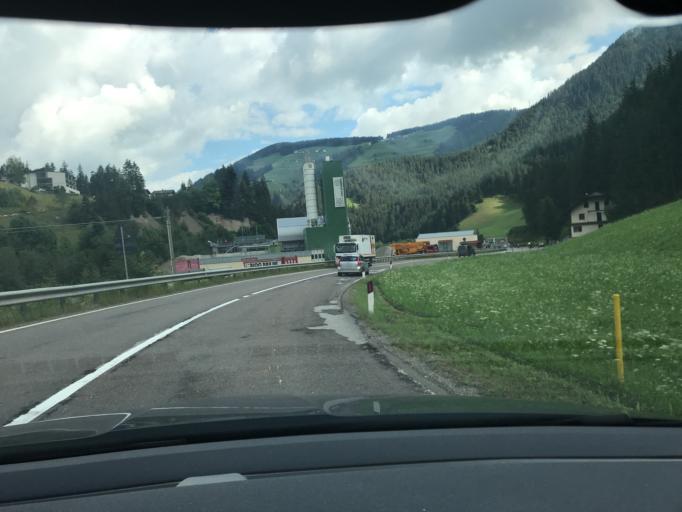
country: IT
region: Trentino-Alto Adige
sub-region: Bolzano
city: San Martino in Badia
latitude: 46.6763
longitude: 11.9009
